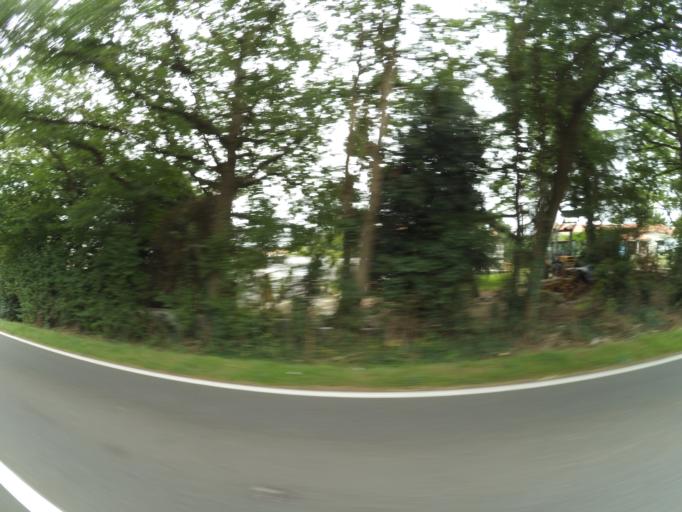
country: FR
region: Pays de la Loire
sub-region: Departement de la Vendee
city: Froidfond
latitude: 46.8714
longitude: -1.7494
